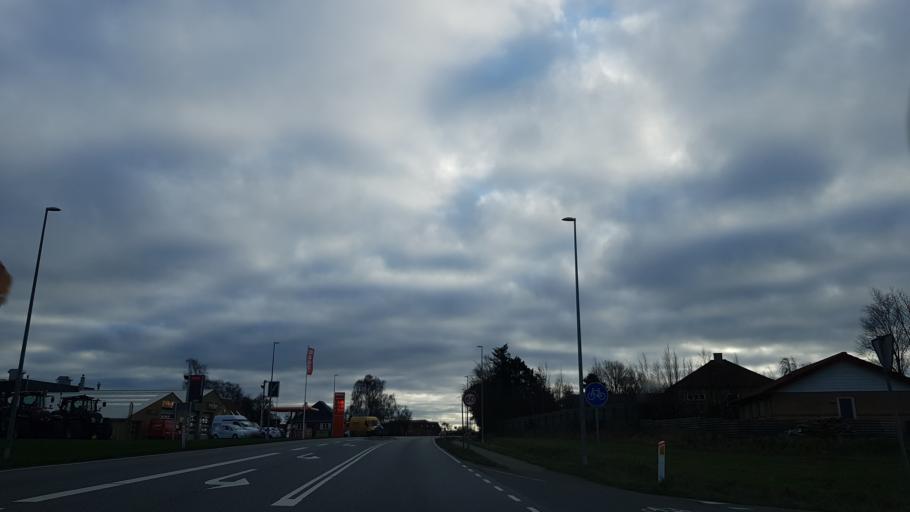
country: DK
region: Zealand
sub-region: Kalundborg Kommune
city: Hong
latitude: 55.4884
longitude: 11.2953
